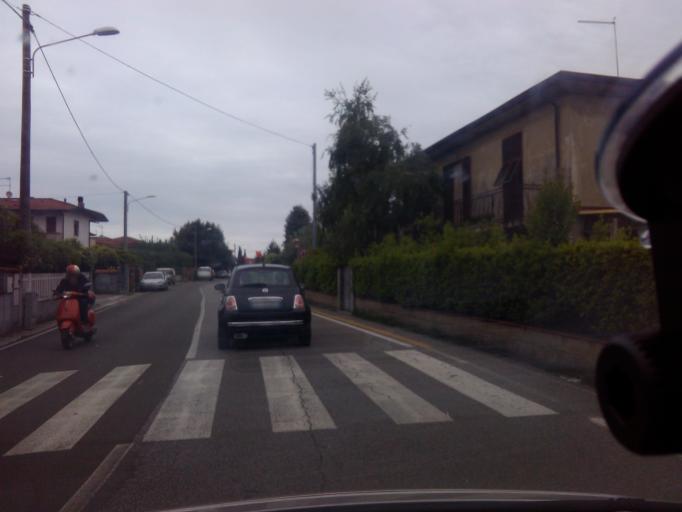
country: IT
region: Tuscany
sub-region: Provincia di Massa-Carrara
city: Massa
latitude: 44.0180
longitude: 10.1126
